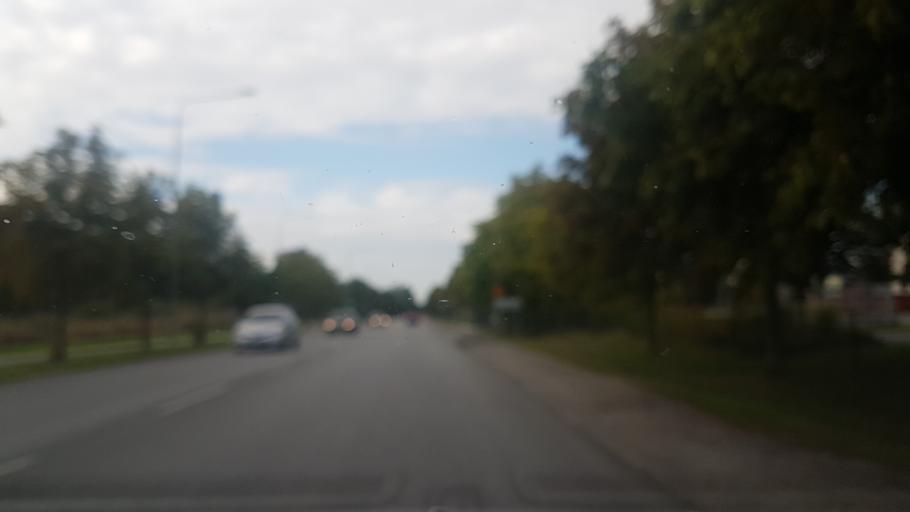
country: SE
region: Stockholm
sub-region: Jarfalla Kommun
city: Jakobsberg
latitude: 59.4158
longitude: 17.8255
